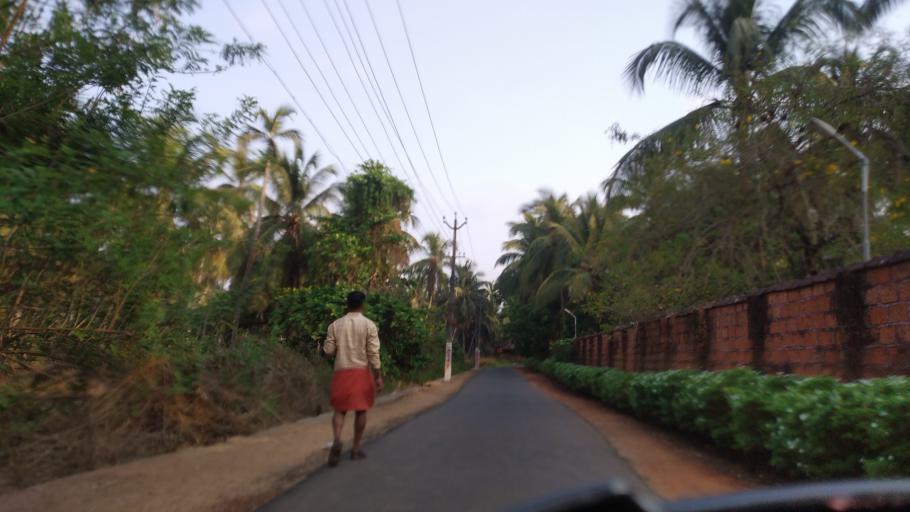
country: IN
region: Kerala
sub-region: Thrissur District
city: Thanniyam
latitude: 10.4243
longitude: 76.0821
